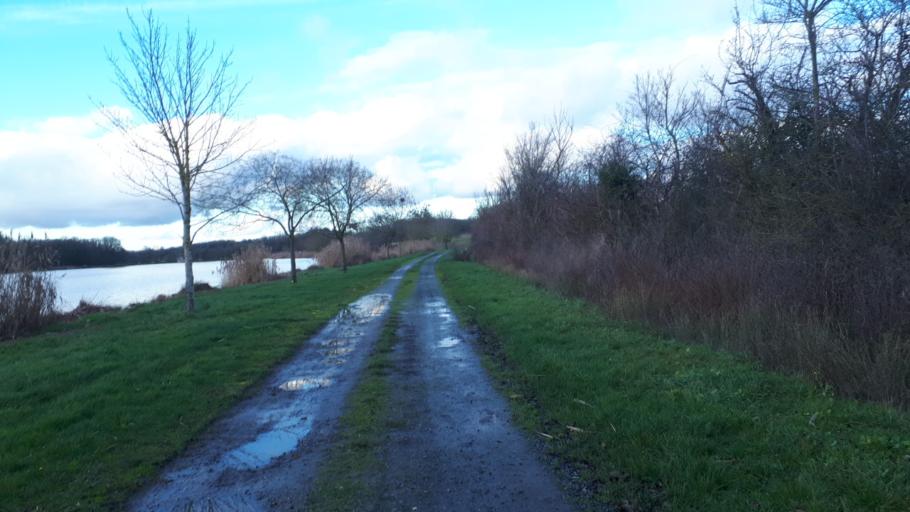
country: FR
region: Poitou-Charentes
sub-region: Departement de la Vienne
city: Pleumartin
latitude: 46.6338
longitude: 0.7661
